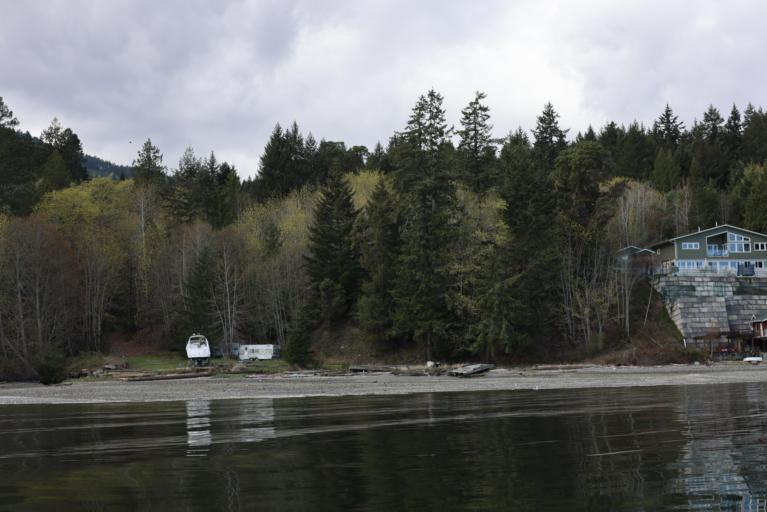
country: CA
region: British Columbia
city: North Saanich
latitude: 48.6027
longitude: -123.5195
